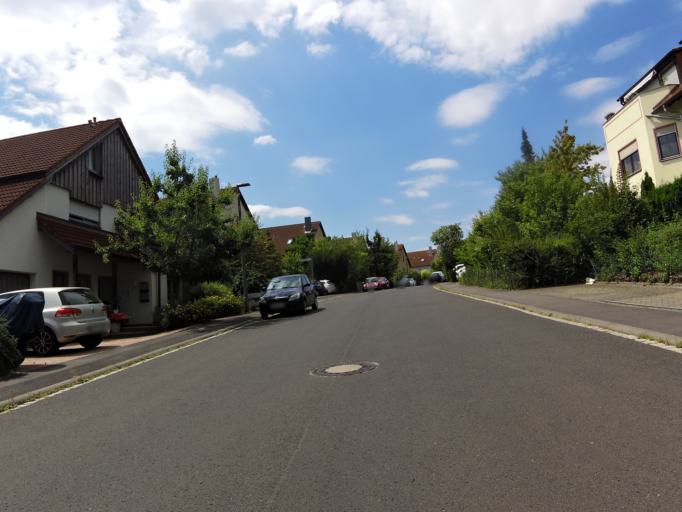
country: DE
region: Bavaria
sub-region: Regierungsbezirk Unterfranken
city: Wuerzburg
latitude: 49.8059
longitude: 9.9736
